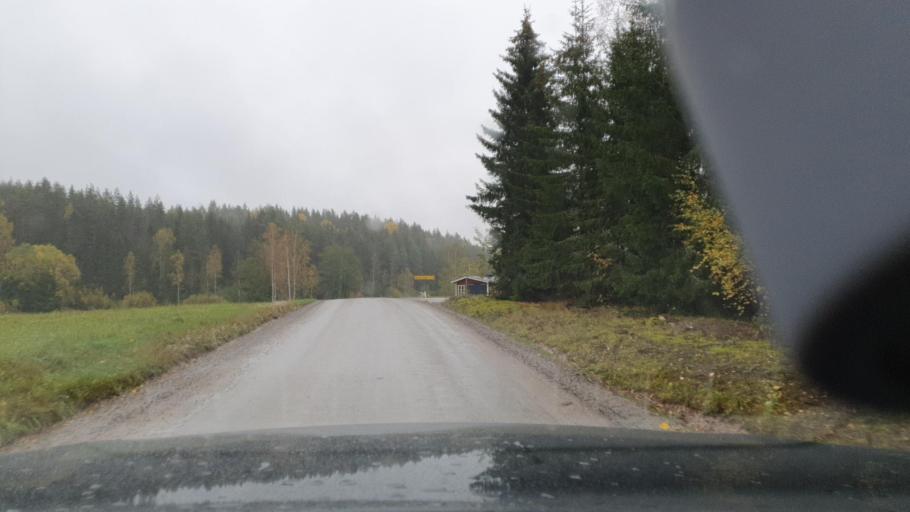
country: SE
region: Vaermland
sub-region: Arvika Kommun
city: Arvika
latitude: 59.6193
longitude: 12.8945
